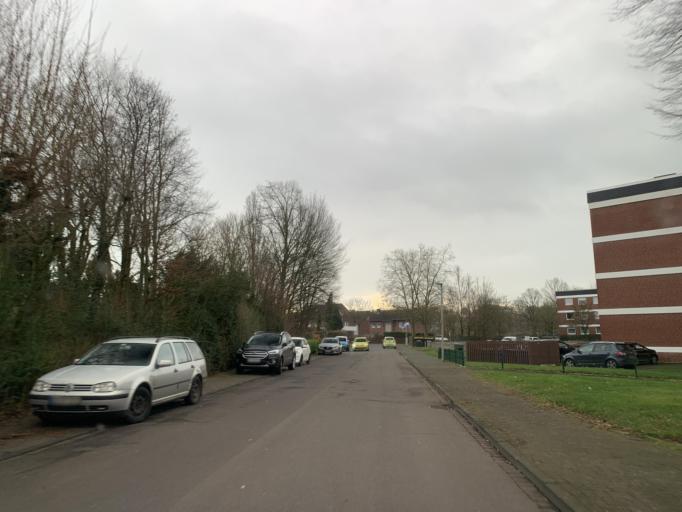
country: DE
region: North Rhine-Westphalia
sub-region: Regierungsbezirk Munster
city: Senden
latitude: 51.8556
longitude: 7.4687
